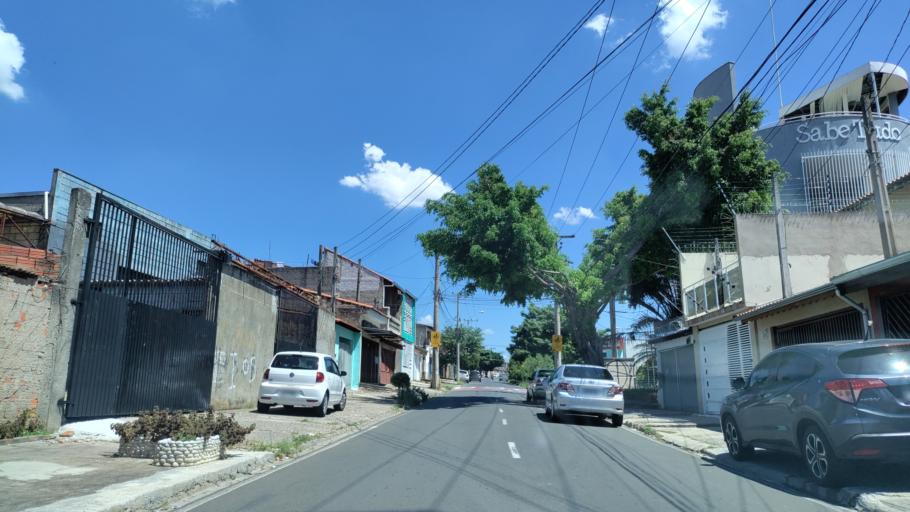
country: BR
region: Sao Paulo
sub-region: Sorocaba
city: Sorocaba
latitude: -23.4576
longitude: -47.4664
